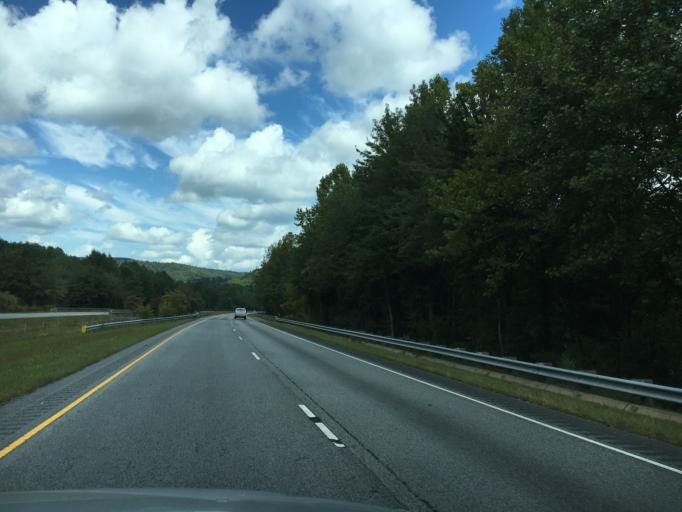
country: US
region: North Carolina
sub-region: Henderson County
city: Flat Rock
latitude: 35.1965
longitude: -82.4507
